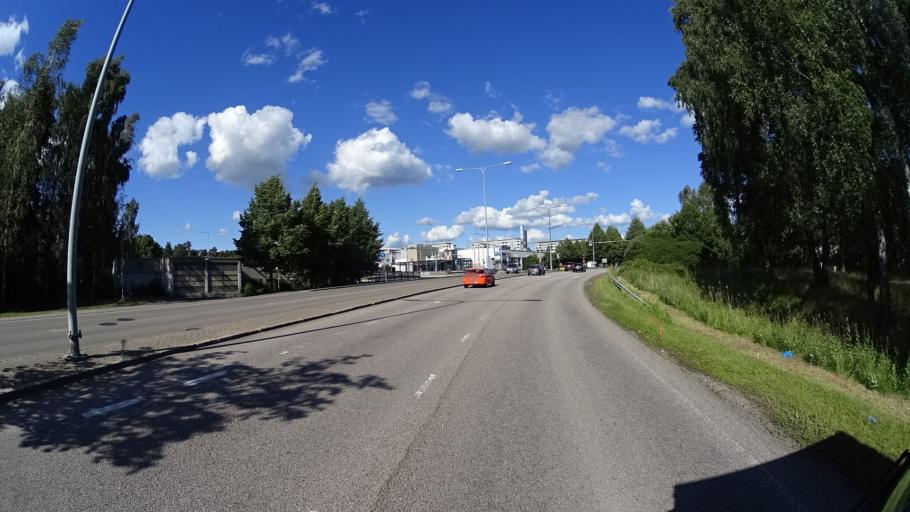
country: FI
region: Uusimaa
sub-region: Helsinki
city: Vantaa
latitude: 60.2346
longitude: 25.0819
